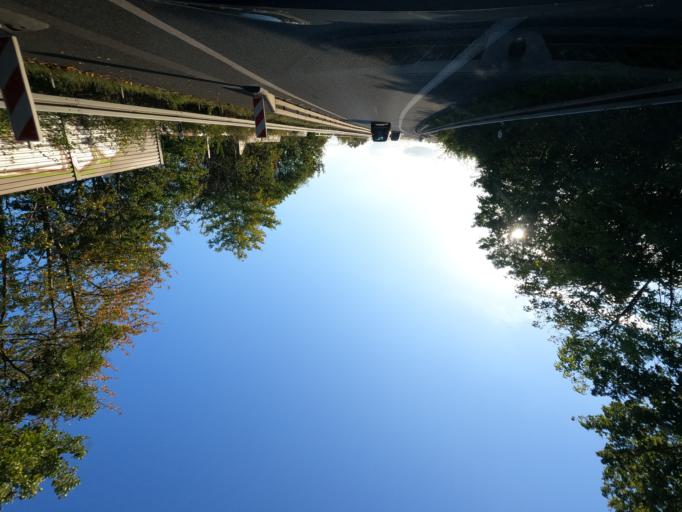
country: DE
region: Lower Saxony
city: Braunschweig
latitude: 52.2837
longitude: 10.4942
